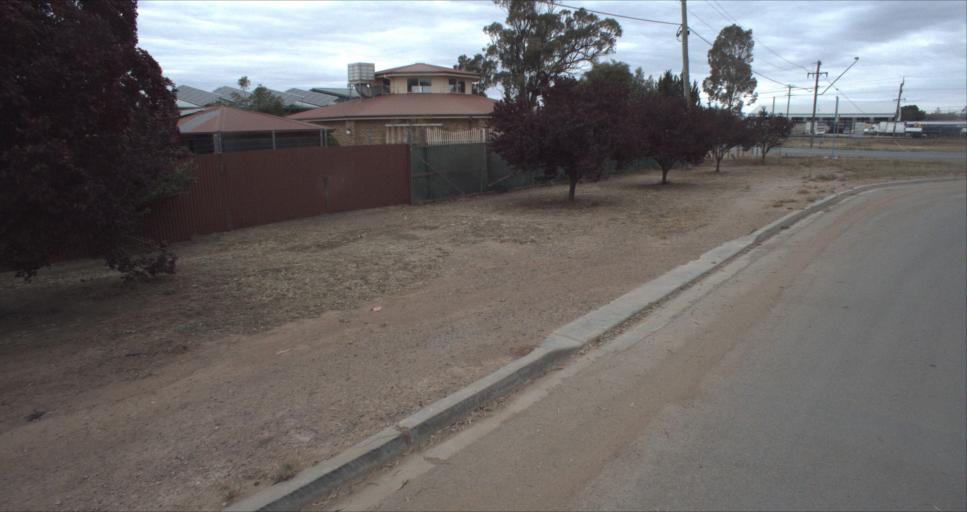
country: AU
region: New South Wales
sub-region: Leeton
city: Leeton
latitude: -34.5507
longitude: 146.3903
